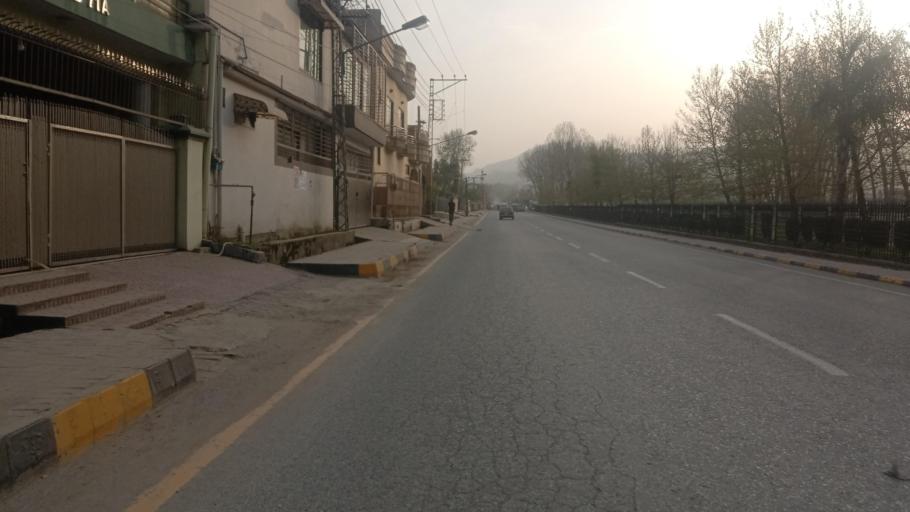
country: PK
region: Khyber Pakhtunkhwa
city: Abbottabad
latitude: 34.1728
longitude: 73.2366
